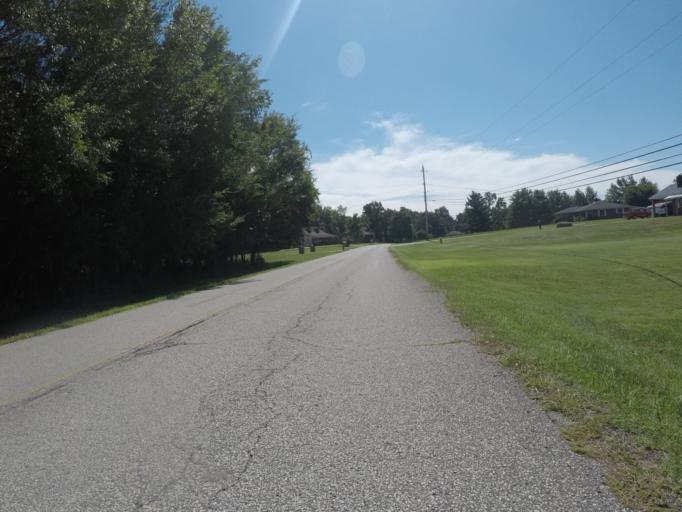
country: US
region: Kentucky
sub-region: Boyd County
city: Meads
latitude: 38.4146
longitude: -82.6592
